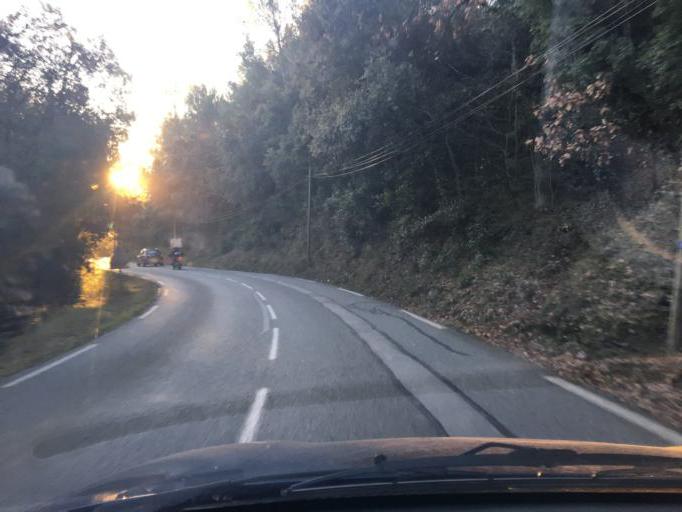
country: FR
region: Provence-Alpes-Cote d'Azur
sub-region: Departement du Var
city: Taradeau
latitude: 43.4574
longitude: 6.4195
